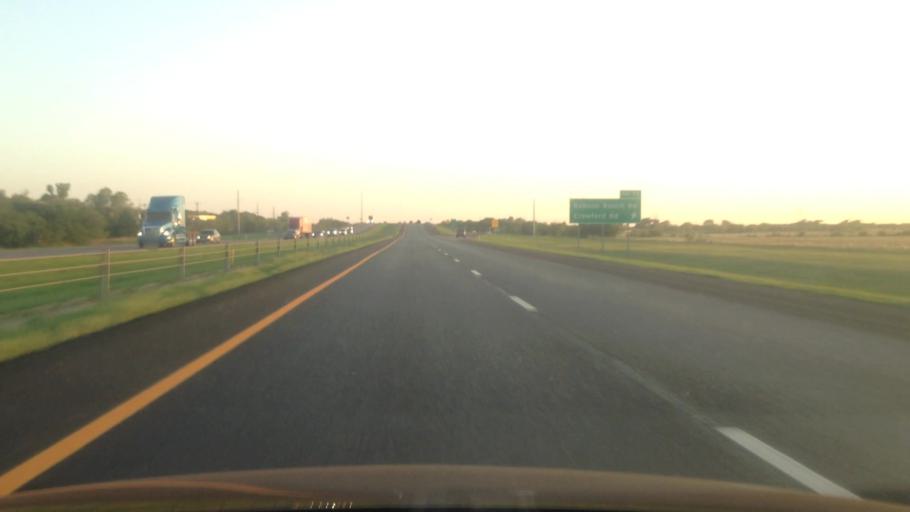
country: US
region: Texas
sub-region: Denton County
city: Argyle
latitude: 33.1359
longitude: -97.2040
